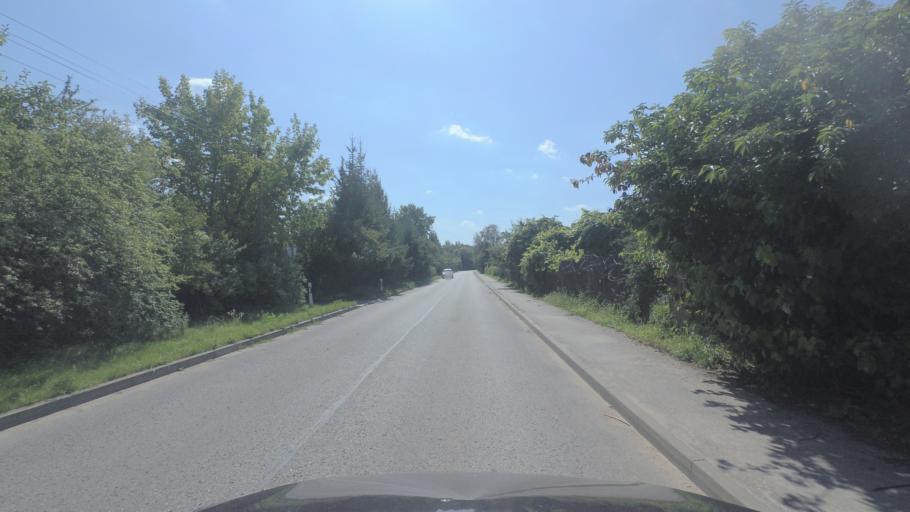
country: LT
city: Nemencine
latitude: 54.8344
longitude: 25.3692
